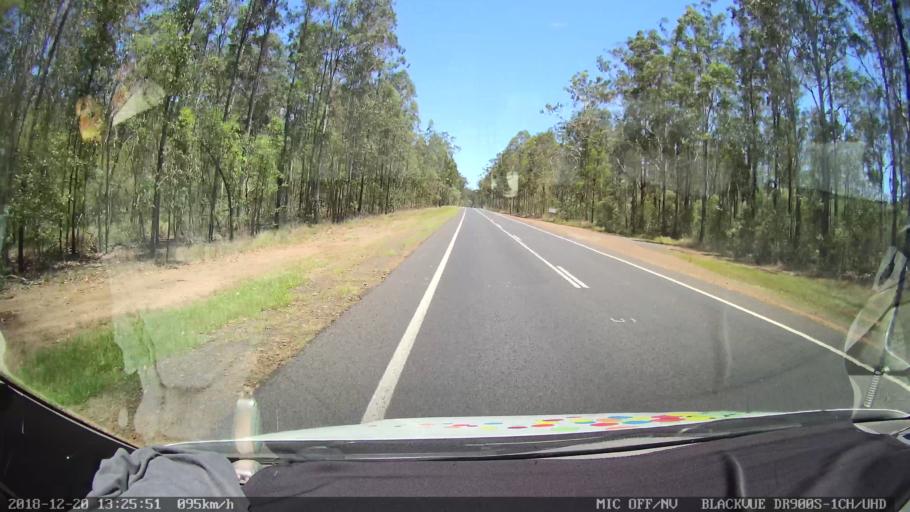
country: AU
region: New South Wales
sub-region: Richmond Valley
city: Casino
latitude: -29.1370
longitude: 152.9959
